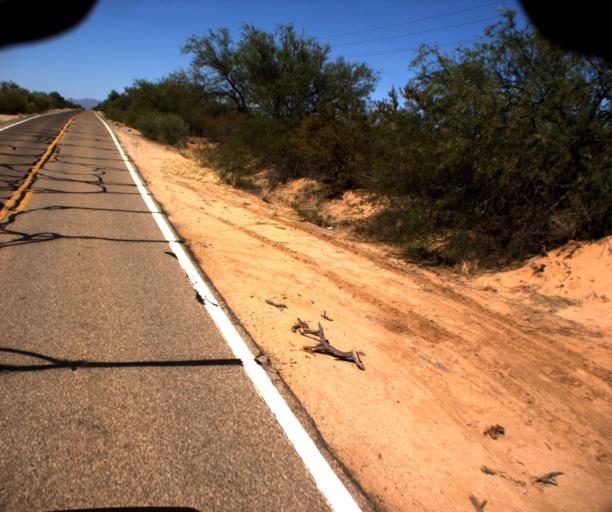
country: US
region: Arizona
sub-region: Pima County
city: Three Points
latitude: 32.0426
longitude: -111.3336
